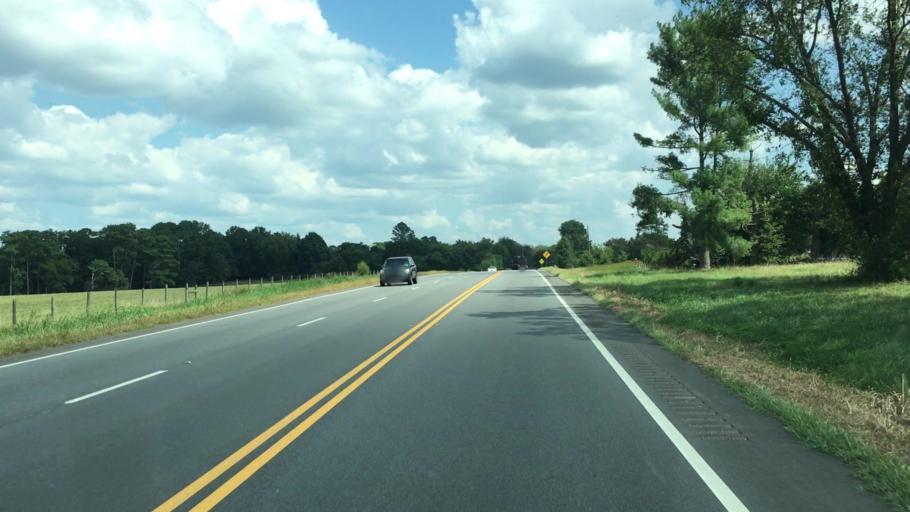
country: US
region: Georgia
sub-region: Putnam County
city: Jefferson
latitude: 33.4724
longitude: -83.4229
